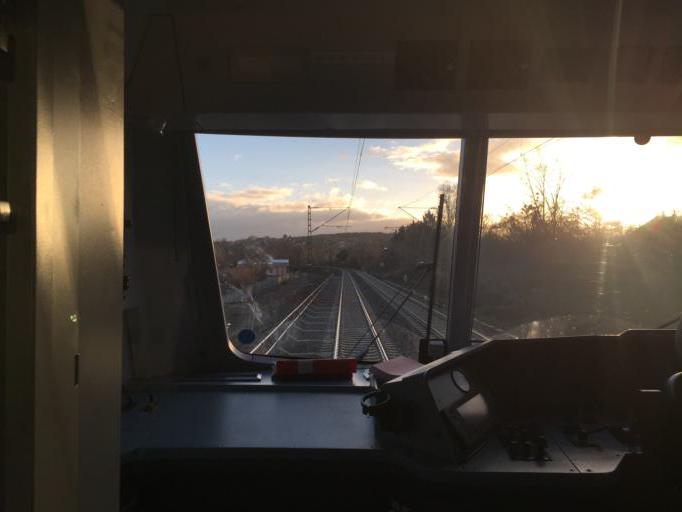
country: DE
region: Hesse
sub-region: Regierungsbezirk Darmstadt
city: Bad Vilbel
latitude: 50.1775
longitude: 8.7251
